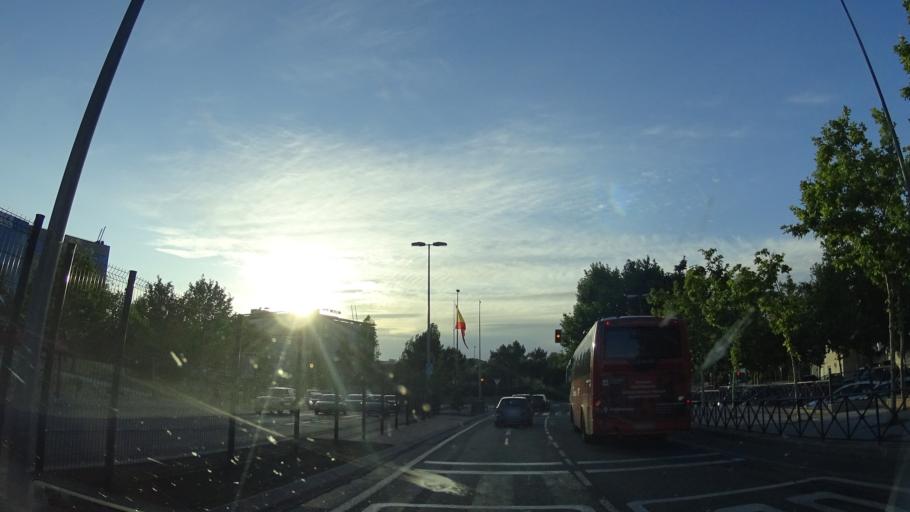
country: ES
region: Madrid
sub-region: Provincia de Madrid
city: San Sebastian de los Reyes
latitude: 40.5363
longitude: -3.6229
